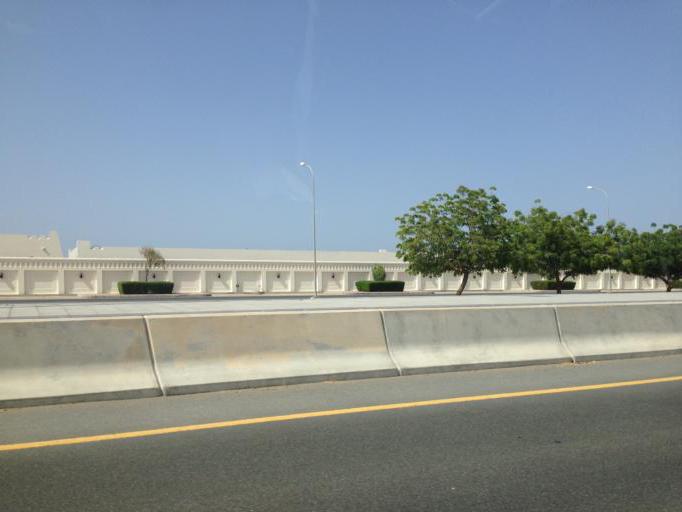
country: OM
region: Muhafazat Masqat
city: Bawshar
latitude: 23.6040
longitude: 58.3311
